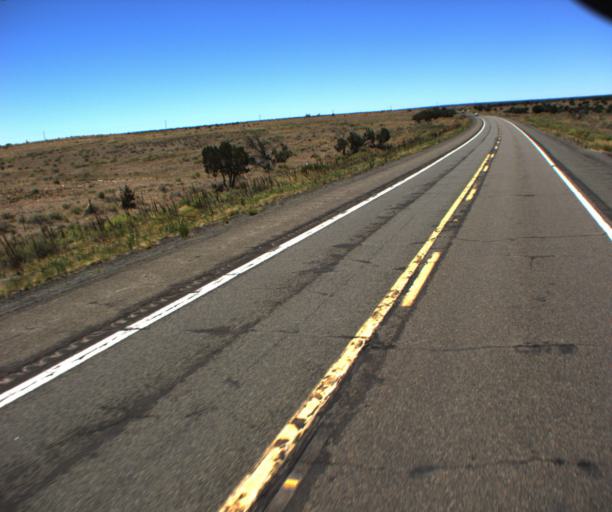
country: US
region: Arizona
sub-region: Coconino County
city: LeChee
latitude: 34.7758
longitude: -111.0046
